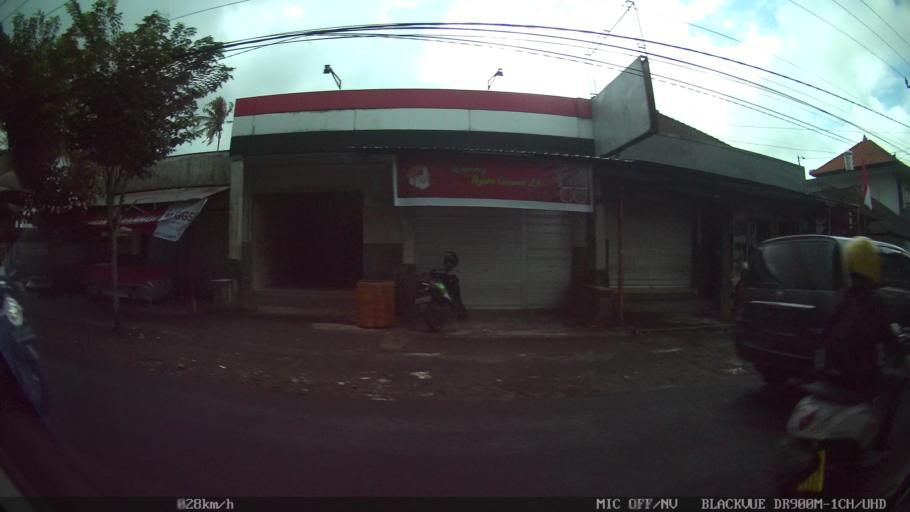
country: ID
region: Bali
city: Banjar Keraman
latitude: -8.5280
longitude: 115.2122
